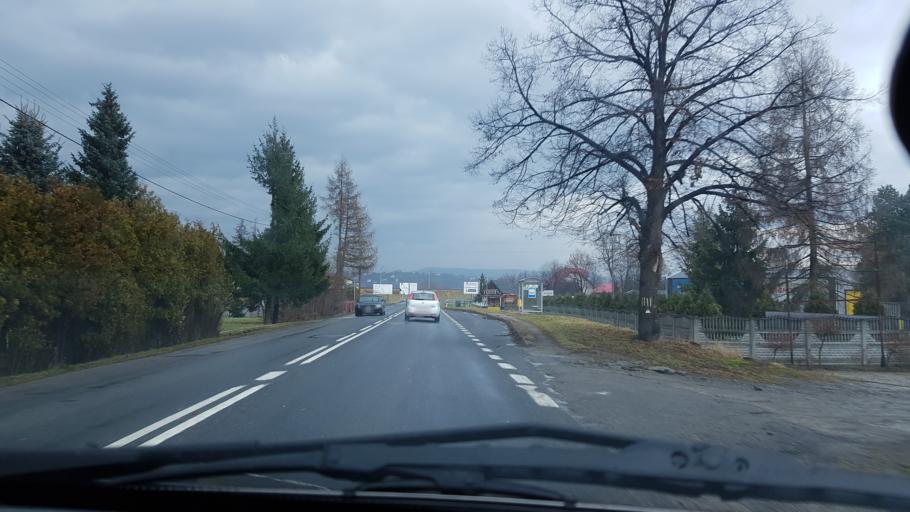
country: PL
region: Silesian Voivodeship
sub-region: Powiat zywiecki
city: Zarzecze
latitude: 49.7091
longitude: 19.1729
